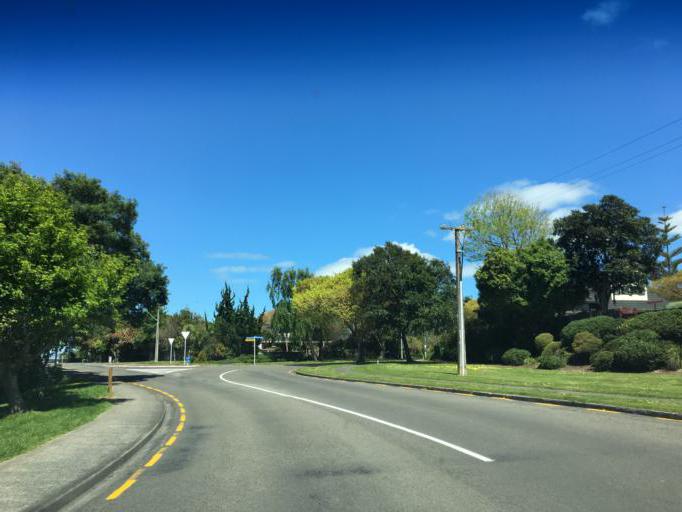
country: NZ
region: Manawatu-Wanganui
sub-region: Palmerston North City
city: Palmerston North
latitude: -40.3773
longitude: 175.5790
